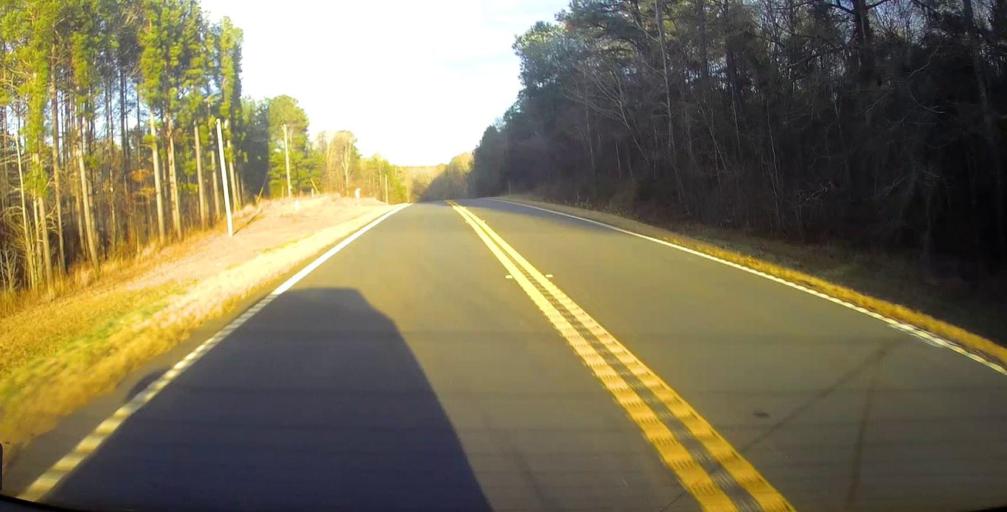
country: US
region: Georgia
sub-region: Talbot County
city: Sardis
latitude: 32.7440
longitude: -84.6008
